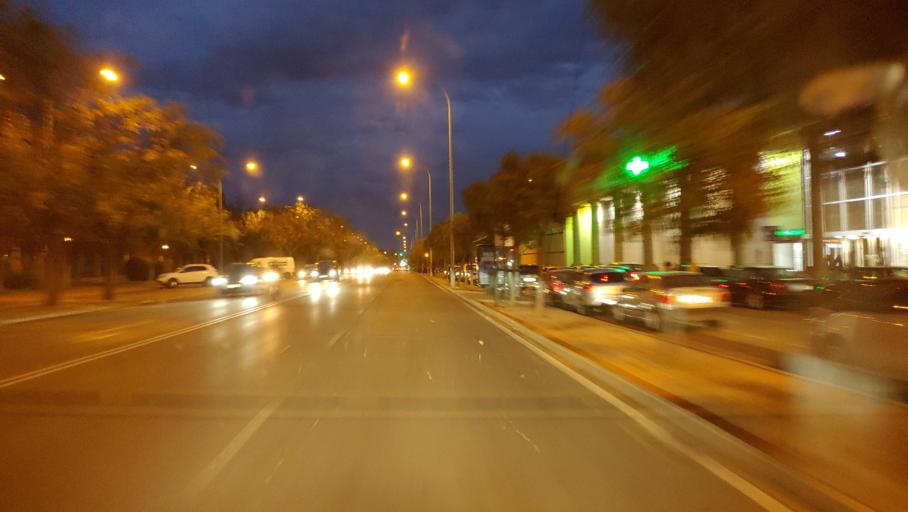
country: ES
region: Castille-La Mancha
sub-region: Provincia de Ciudad Real
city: Ciudad Real
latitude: 38.9806
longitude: -3.9165
